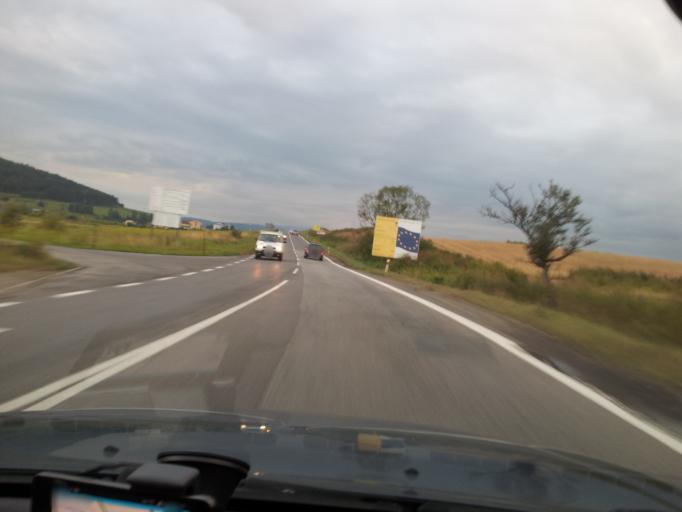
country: SK
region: Presovsky
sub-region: Okres Poprad
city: Poprad
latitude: 49.1038
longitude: 20.3446
